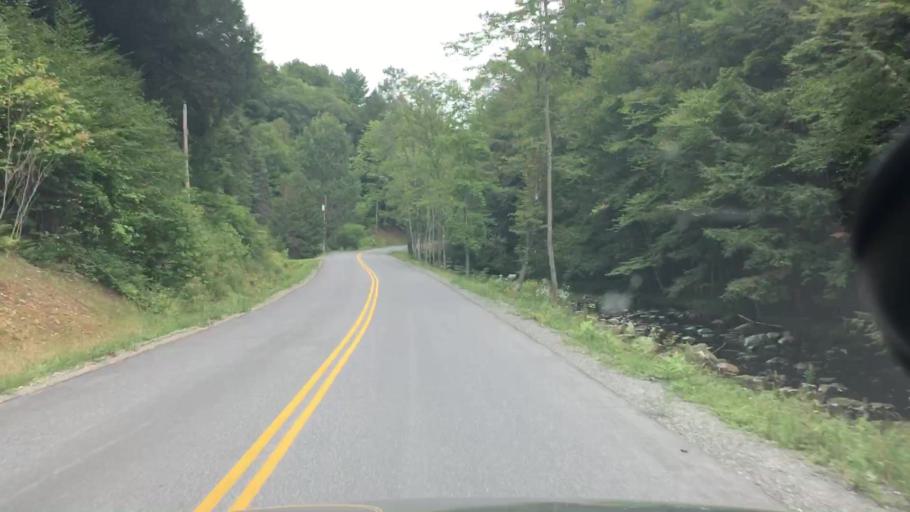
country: US
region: Massachusetts
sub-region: Franklin County
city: Colrain
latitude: 42.7667
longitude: -72.7649
